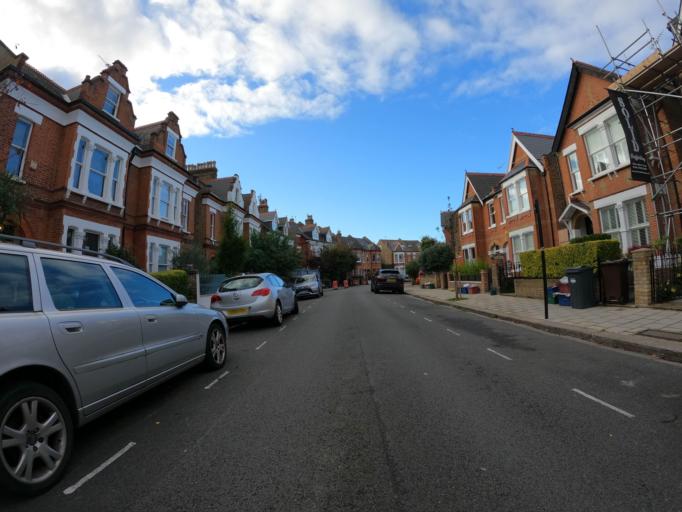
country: GB
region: England
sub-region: Greater London
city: Acton
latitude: 51.4854
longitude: -0.2737
